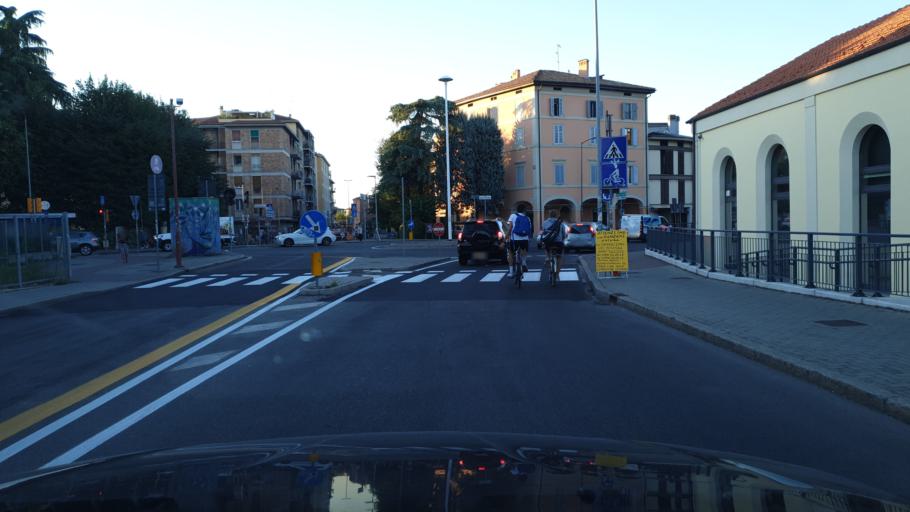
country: IT
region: Emilia-Romagna
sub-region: Provincia di Bologna
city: Bologna
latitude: 44.4992
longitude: 11.3595
